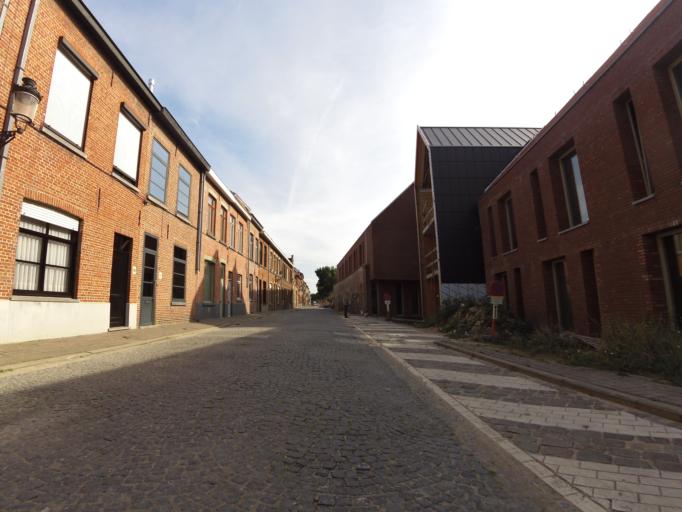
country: BE
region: Flanders
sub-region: Provincie West-Vlaanderen
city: Brugge
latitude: 51.2195
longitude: 3.2317
